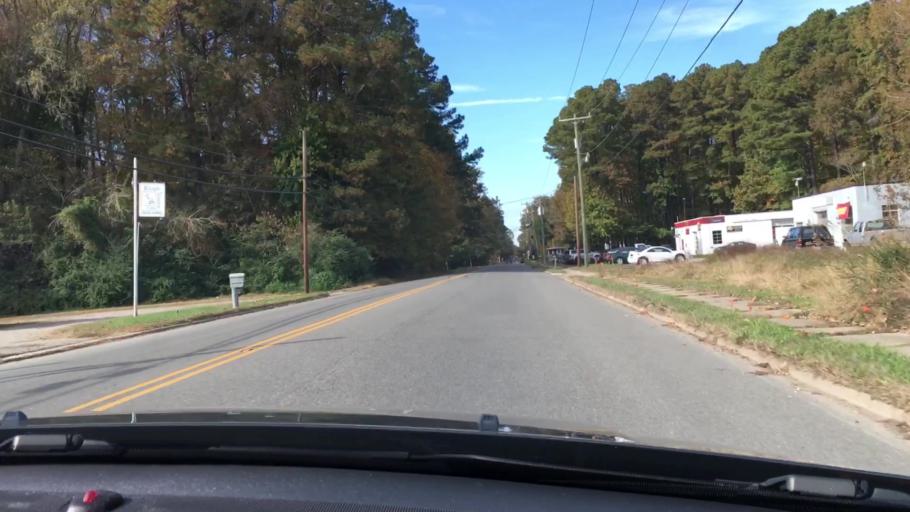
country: US
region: Virginia
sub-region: King William County
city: West Point
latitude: 37.5578
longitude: -76.8189
